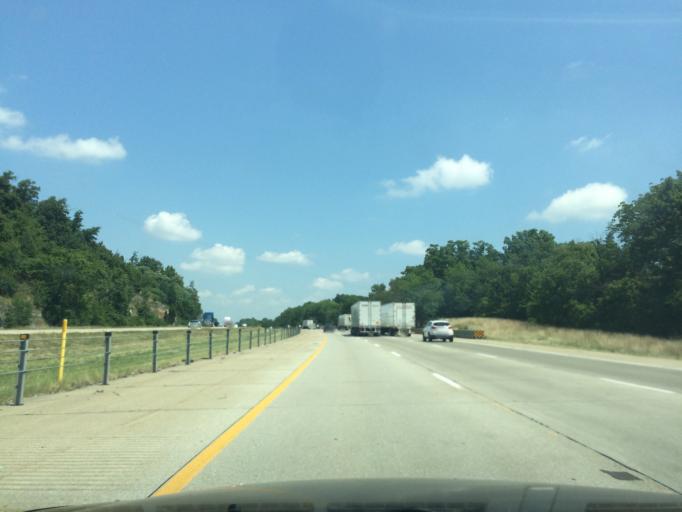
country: US
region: Kentucky
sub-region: Bullitt County
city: Shepherdsville
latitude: 38.0111
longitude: -85.6969
